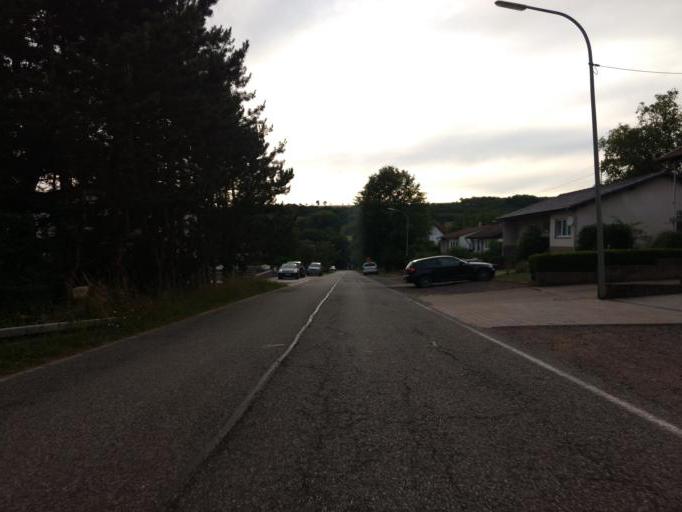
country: FR
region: Lorraine
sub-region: Departement de la Moselle
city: Bouzonville
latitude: 49.3244
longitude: 6.6086
